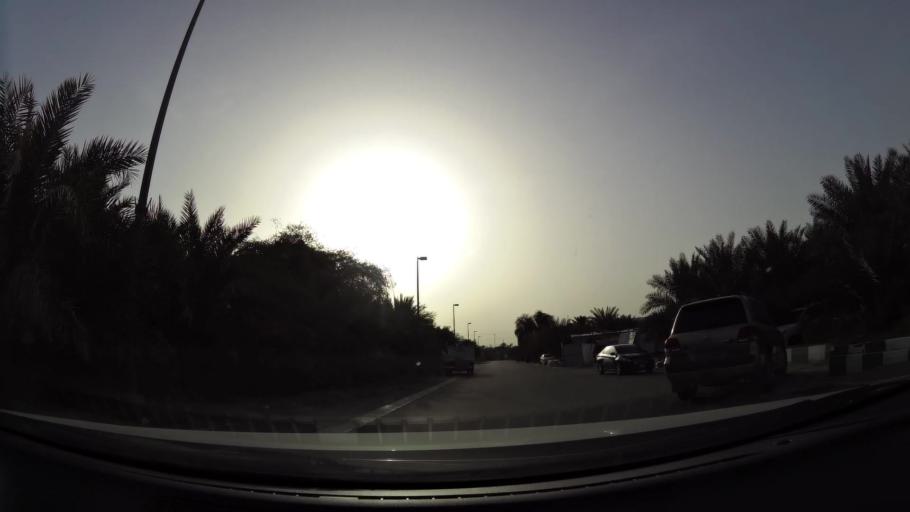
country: AE
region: Abu Dhabi
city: Al Ain
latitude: 24.1168
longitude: 55.7119
